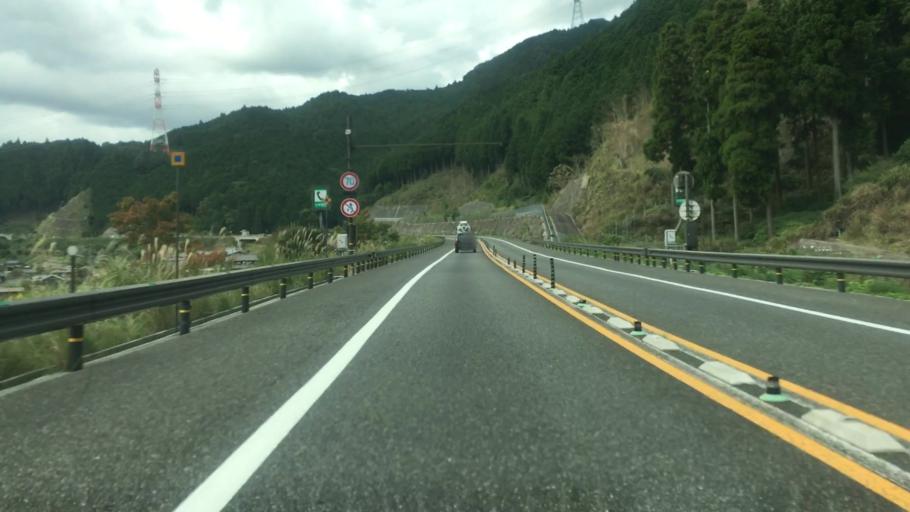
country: JP
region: Kyoto
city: Fukuchiyama
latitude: 35.2813
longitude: 134.9861
